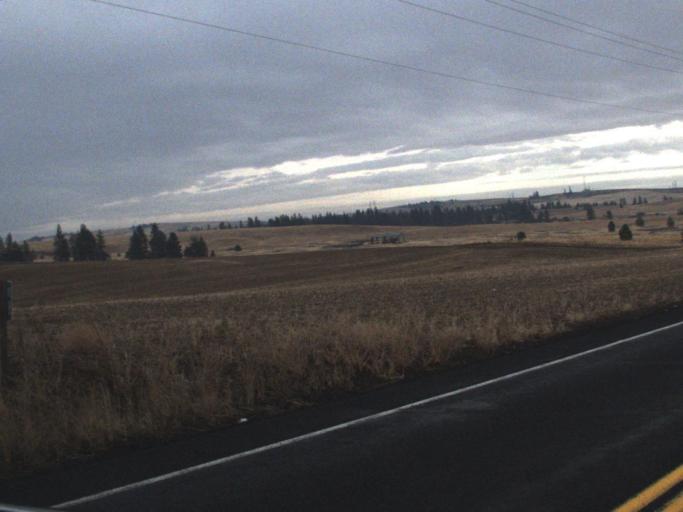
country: US
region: Washington
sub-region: Lincoln County
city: Davenport
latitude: 47.7641
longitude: -118.1735
